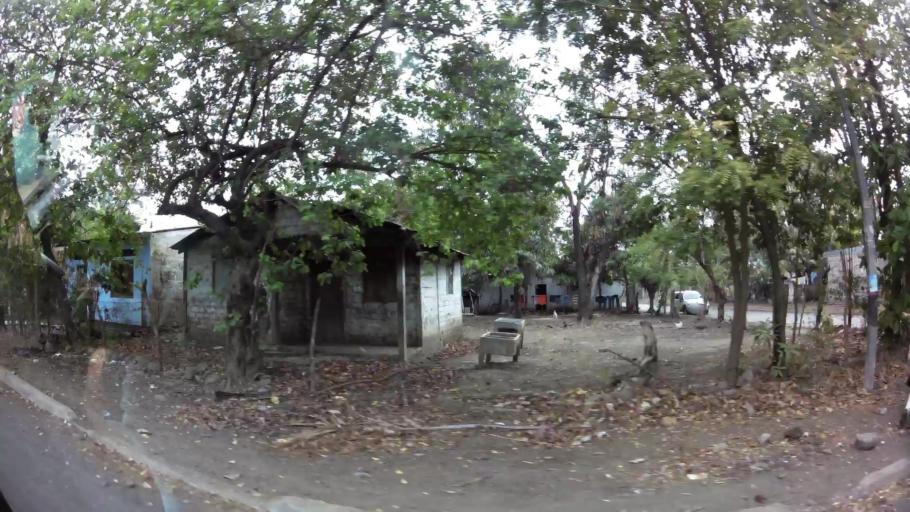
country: NI
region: Chinandega
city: Chinandega
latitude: 12.6158
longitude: -87.1137
